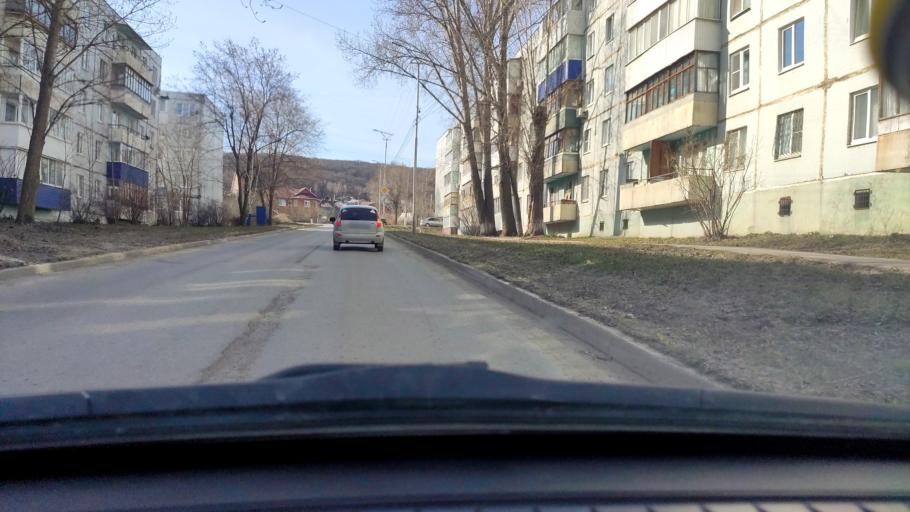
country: RU
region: Samara
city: Zhigulevsk
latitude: 53.3958
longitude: 49.4974
